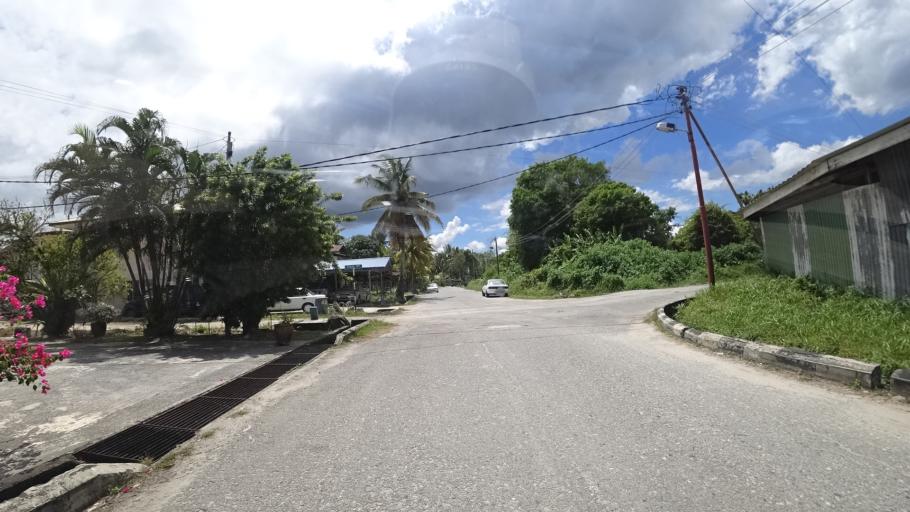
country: BN
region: Brunei and Muara
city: Bandar Seri Begawan
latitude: 4.8550
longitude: 114.8937
